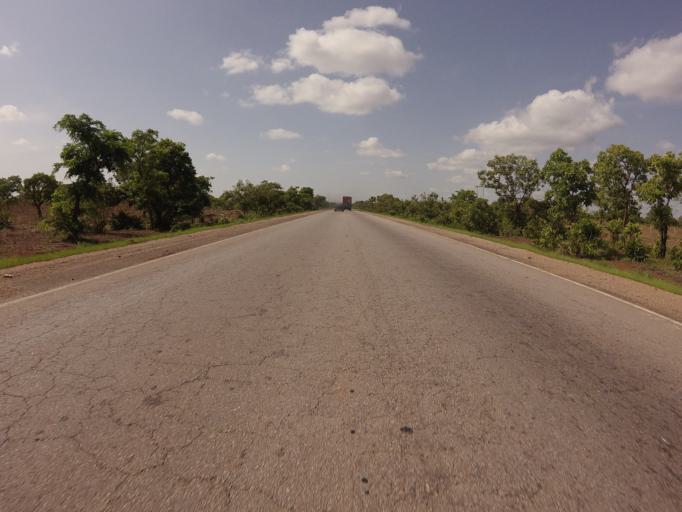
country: GH
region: Northern
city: Savelugu
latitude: 9.9502
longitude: -0.8368
